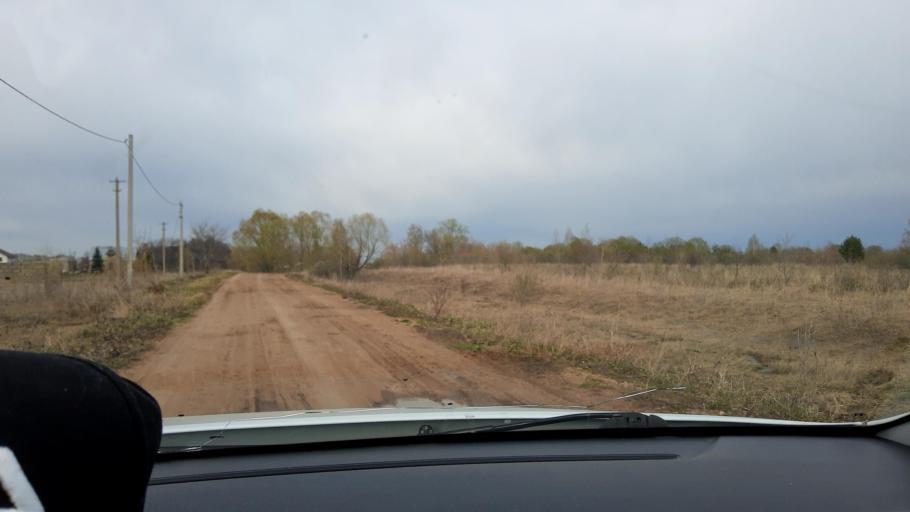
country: RU
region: Bashkortostan
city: Iglino
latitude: 54.8056
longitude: 56.4380
